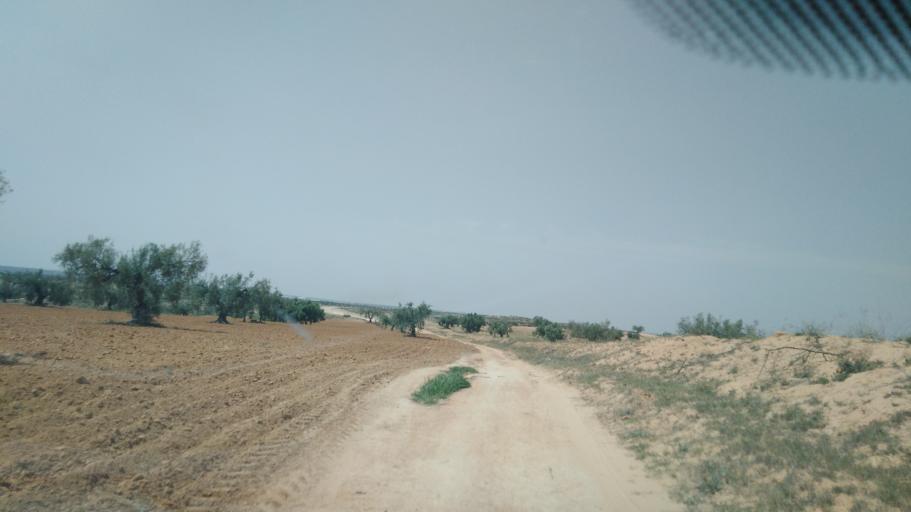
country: TN
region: Safaqis
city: Sfax
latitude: 34.7611
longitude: 10.5754
